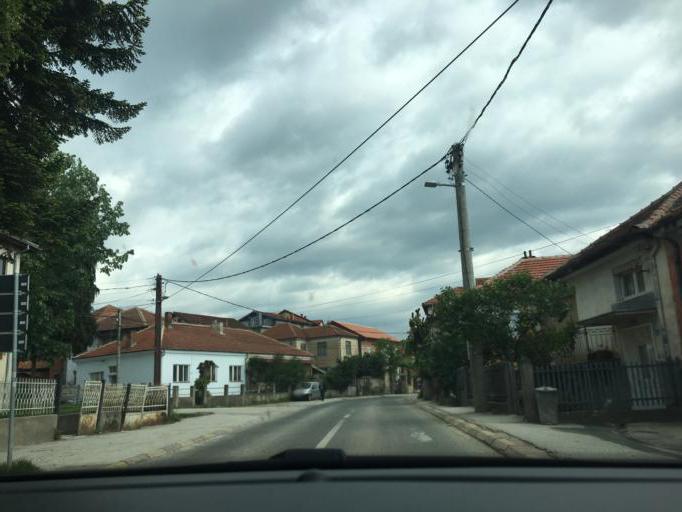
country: MK
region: Resen
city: Resen
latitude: 41.0898
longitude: 21.0094
